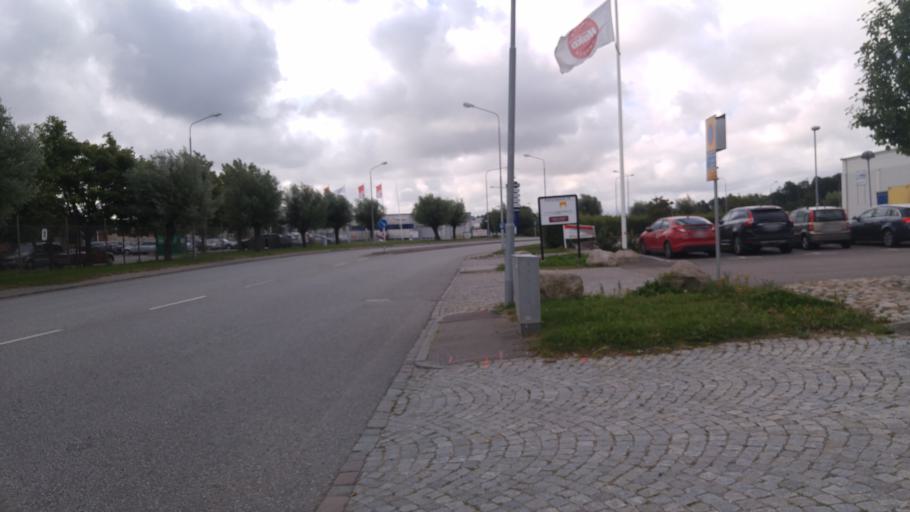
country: SE
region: Skane
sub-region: Malmo
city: Oxie
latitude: 55.5557
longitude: 13.0462
